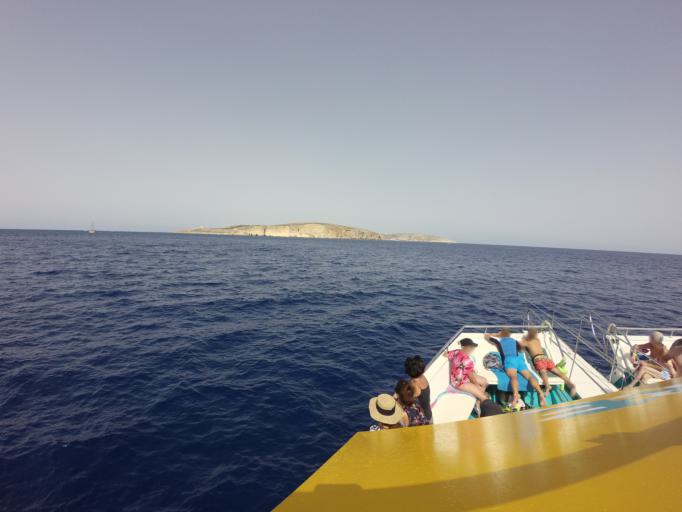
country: MT
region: Il-Mellieha
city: Mellieha
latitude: 36.0038
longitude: 14.3612
